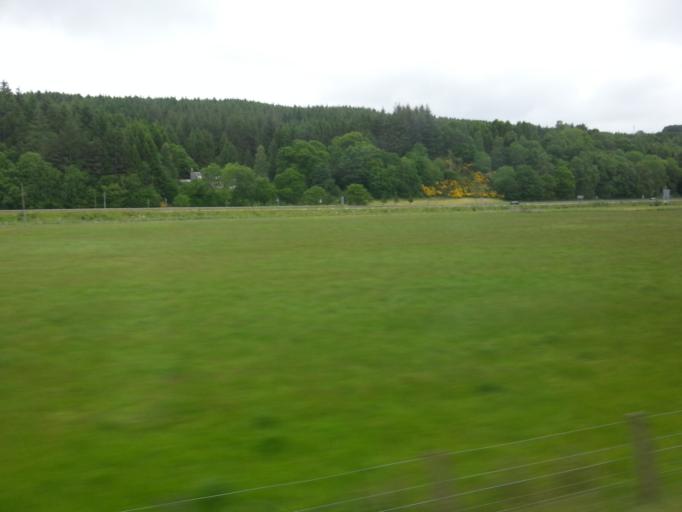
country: GB
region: Scotland
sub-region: Perth and Kinross
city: Pitlochry
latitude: 56.6454
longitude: -3.6615
